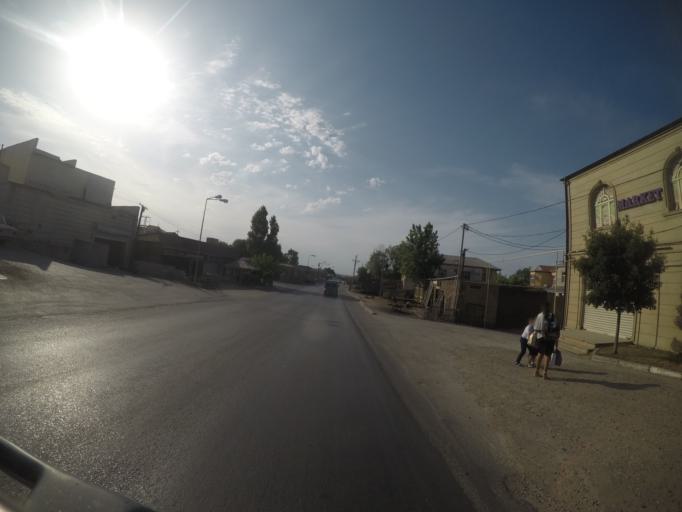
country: AZ
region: Baki
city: Binagadi
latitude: 40.4715
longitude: 49.8367
